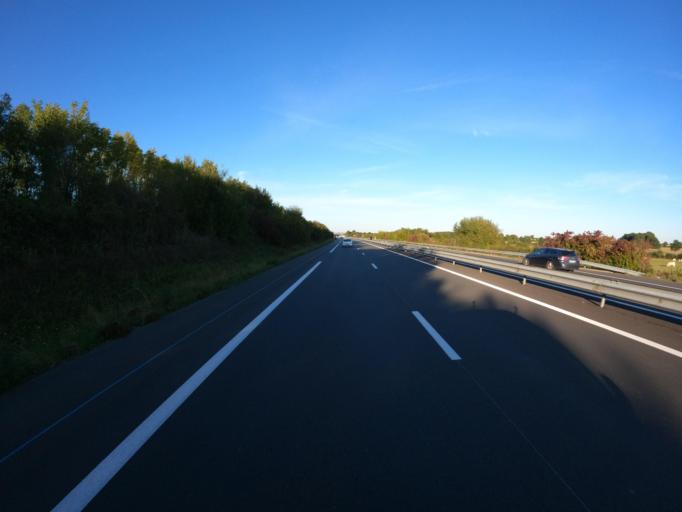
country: FR
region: Pays de la Loire
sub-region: Departement de la Vendee
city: Saint-Fulgent
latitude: 46.8224
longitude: -1.1778
